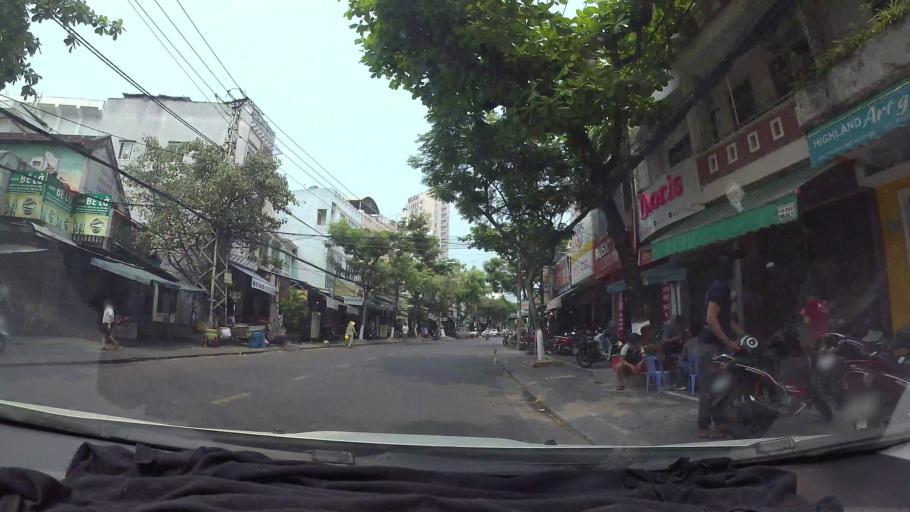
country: VN
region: Da Nang
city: Da Nang
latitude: 16.0590
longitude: 108.2213
